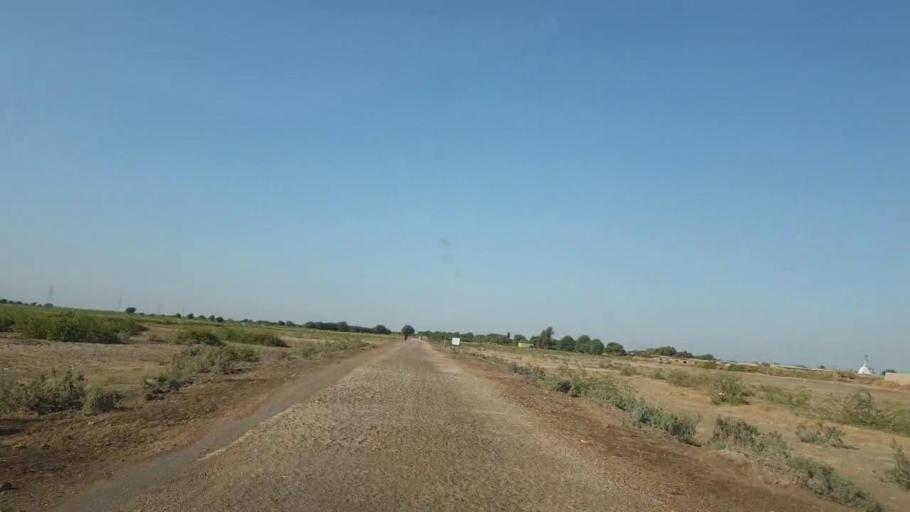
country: PK
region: Sindh
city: Kunri
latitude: 25.0436
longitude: 69.4420
